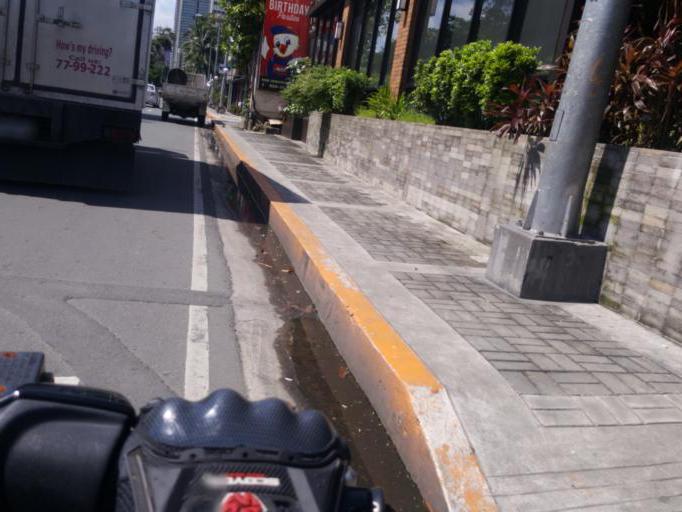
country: PH
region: Metro Manila
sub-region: City of Manila
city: Port Area
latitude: 14.5689
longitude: 120.9834
